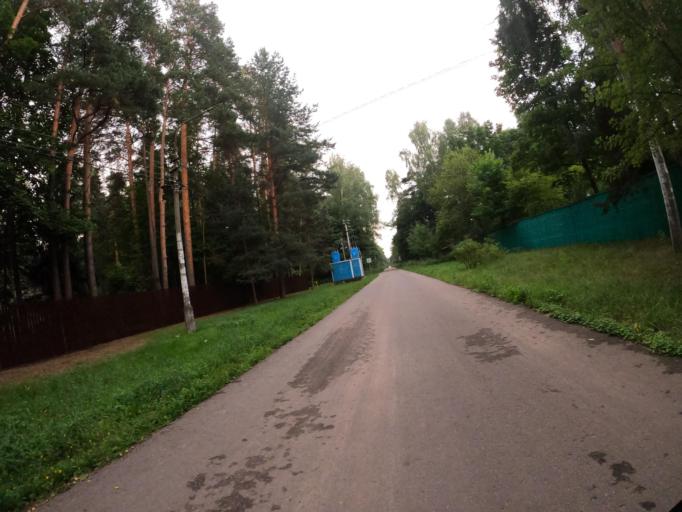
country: RU
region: Moskovskaya
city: Rodniki
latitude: 55.6424
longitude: 38.0676
